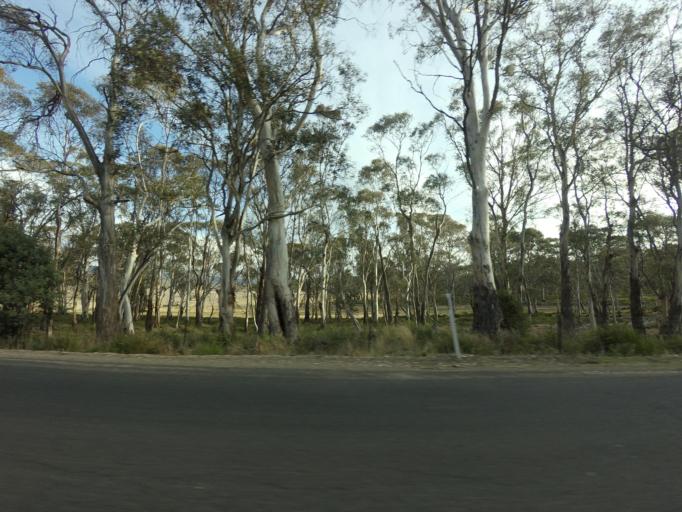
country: AU
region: Tasmania
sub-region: Brighton
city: Bridgewater
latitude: -42.3924
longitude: 147.0452
